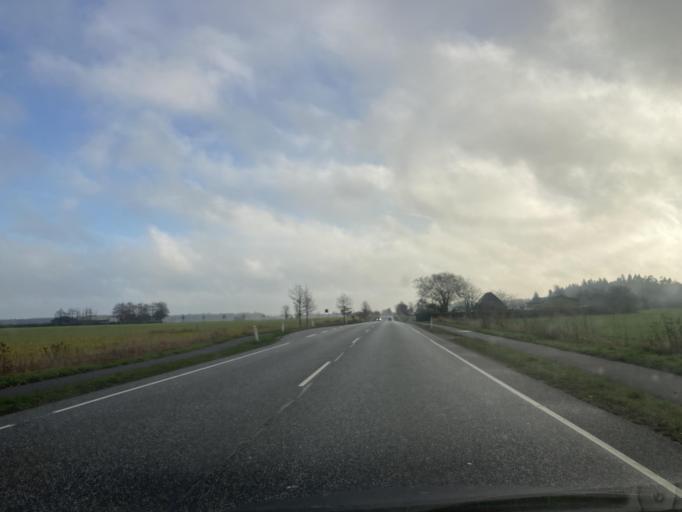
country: DK
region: Zealand
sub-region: Lolland Kommune
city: Maribo
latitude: 54.8021
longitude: 11.4463
